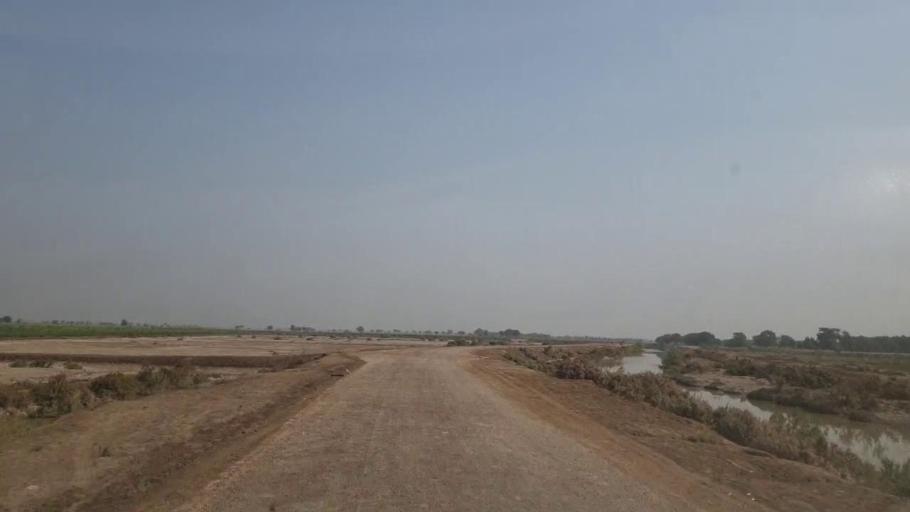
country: PK
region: Sindh
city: Mirpur Khas
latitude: 25.5365
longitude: 69.0737
